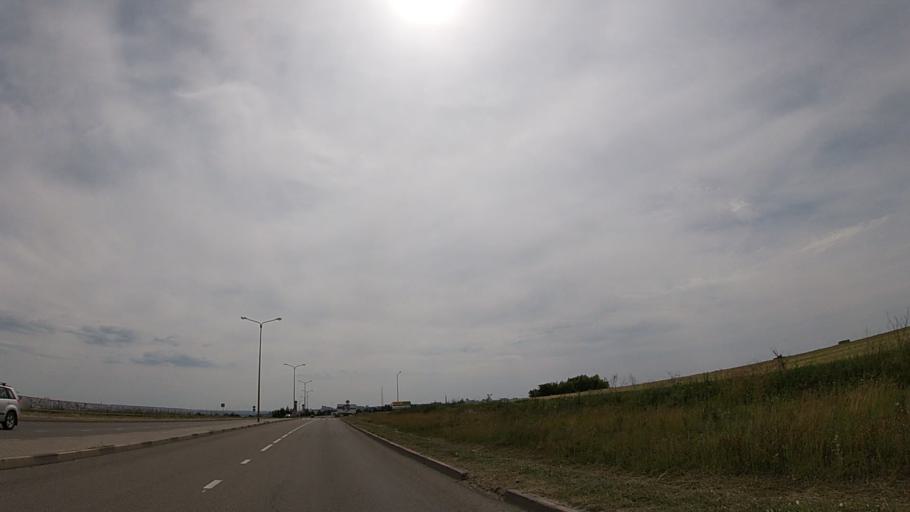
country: RU
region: Belgorod
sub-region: Belgorodskiy Rayon
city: Belgorod
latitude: 50.5944
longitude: 36.5252
